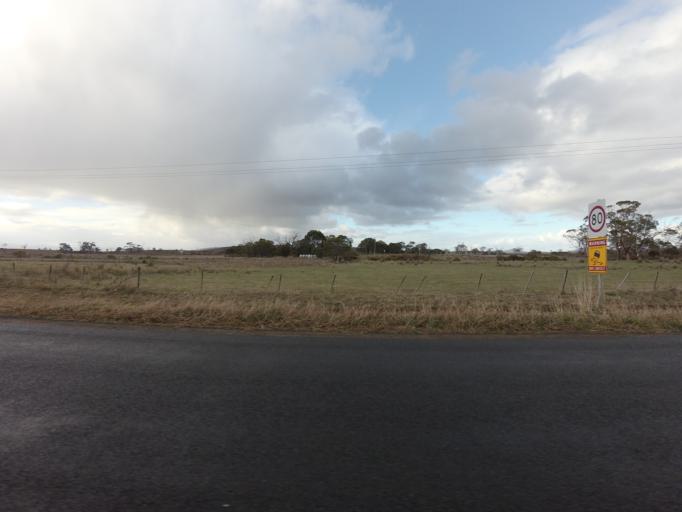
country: AU
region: Tasmania
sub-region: Break O'Day
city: St Helens
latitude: -42.0914
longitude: 148.0782
